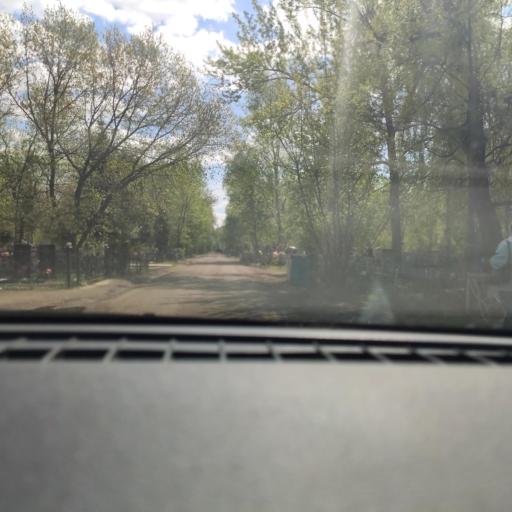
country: RU
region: Voronezj
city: Somovo
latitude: 51.6612
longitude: 39.2954
